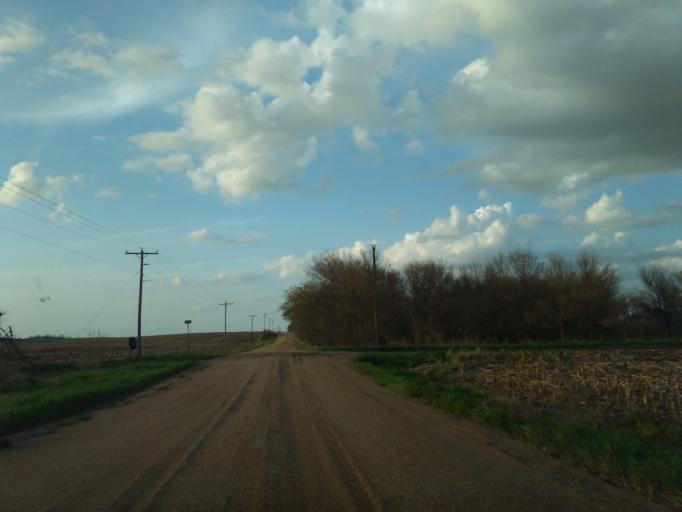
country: US
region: Nebraska
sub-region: Webster County
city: Red Cloud
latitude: 40.2049
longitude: -98.4059
